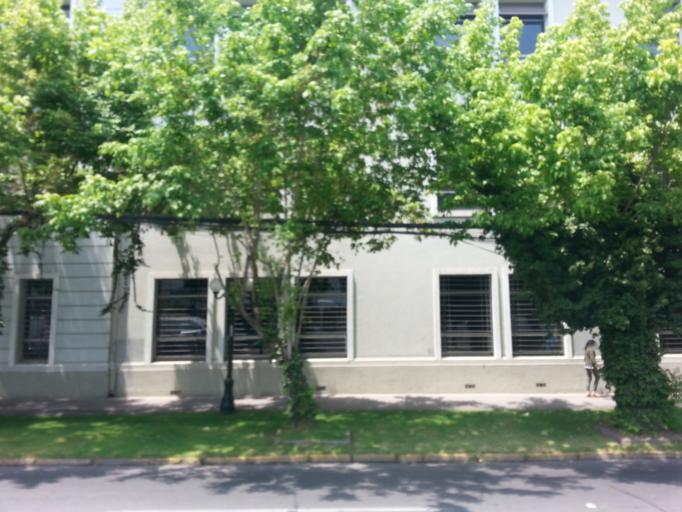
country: CL
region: Santiago Metropolitan
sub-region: Provincia de Santiago
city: Santiago
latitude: -33.4327
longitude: -70.6153
